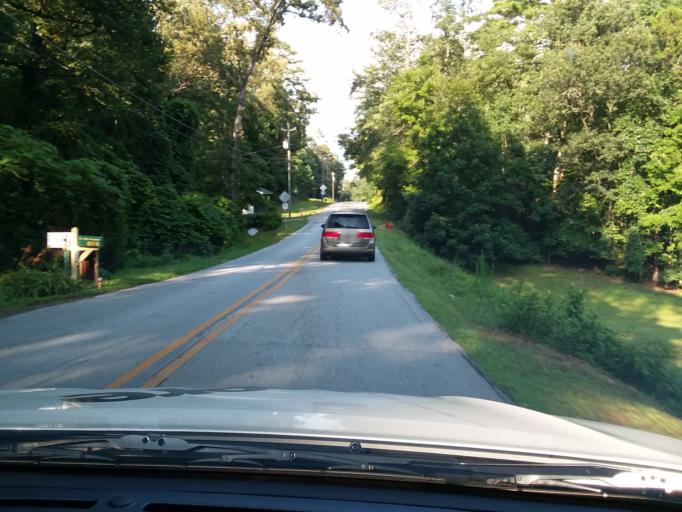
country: US
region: Georgia
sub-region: Rabun County
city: Clayton
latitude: 34.7741
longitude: -83.4230
